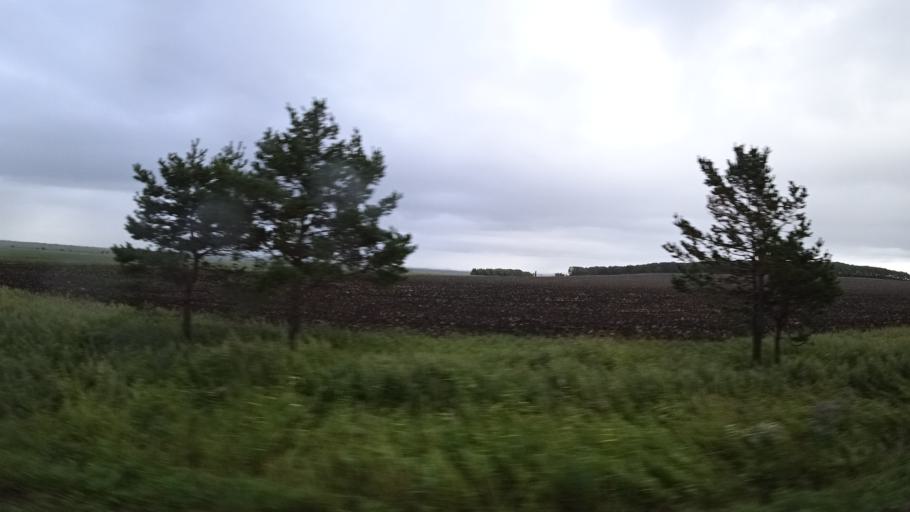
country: RU
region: Primorskiy
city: Chernigovka
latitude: 44.3713
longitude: 132.5302
